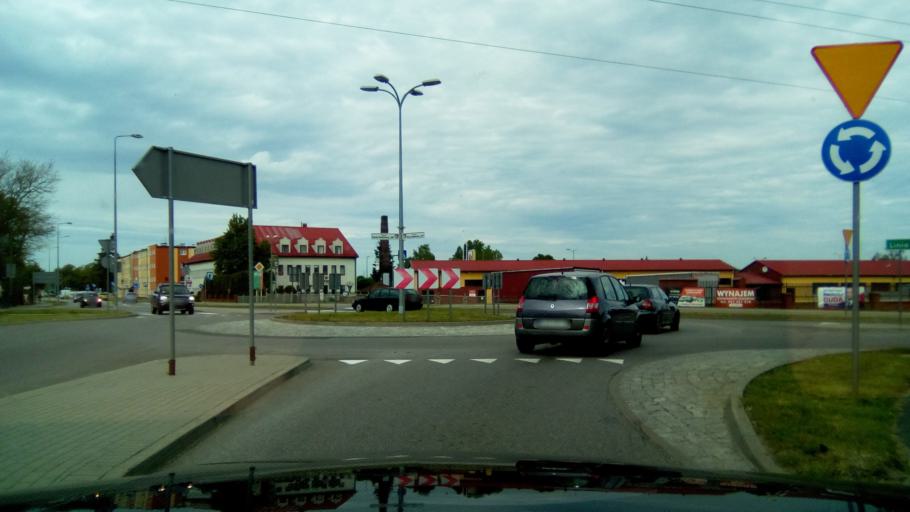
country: PL
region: Pomeranian Voivodeship
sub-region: Powiat leborski
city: Lebork
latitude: 54.5295
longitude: 17.7637
